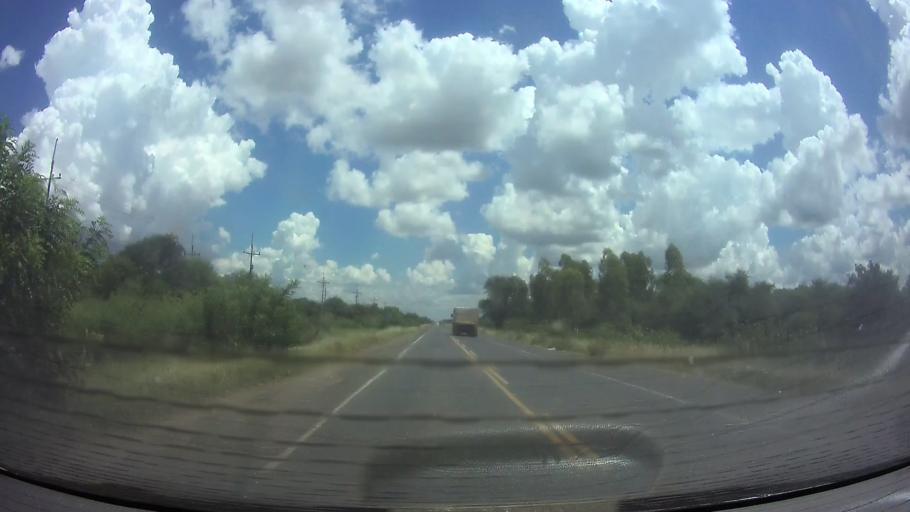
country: PY
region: Central
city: Colonia Mariano Roque Alonso
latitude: -25.1804
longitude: -57.5879
